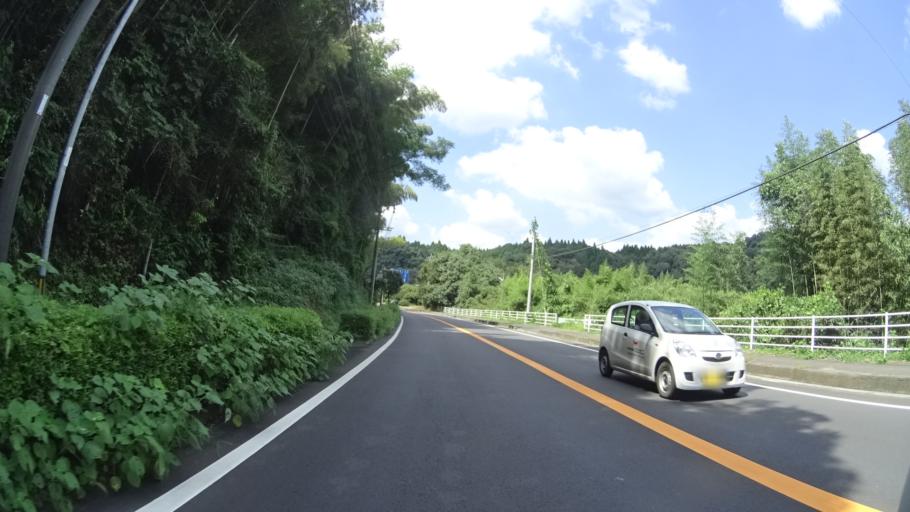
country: JP
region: Kagoshima
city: Kokubu-matsuki
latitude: 31.8579
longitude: 130.7609
